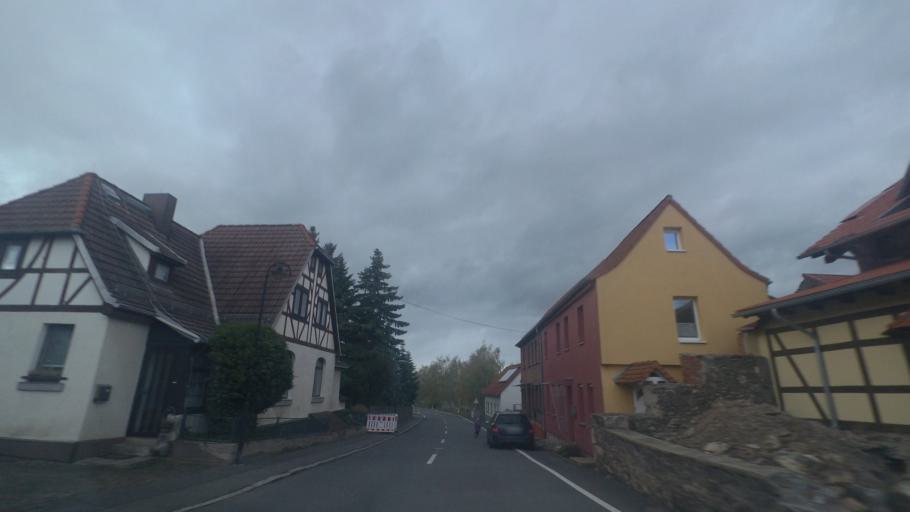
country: DE
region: Thuringia
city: Wernburg
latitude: 50.6794
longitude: 11.5982
